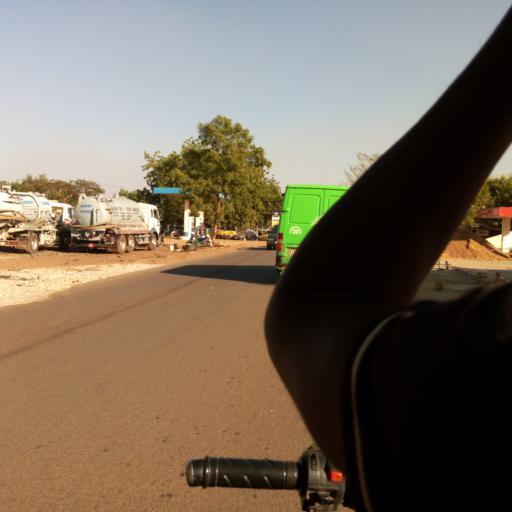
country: ML
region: Bamako
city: Bamako
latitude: 12.6540
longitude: -8.0209
